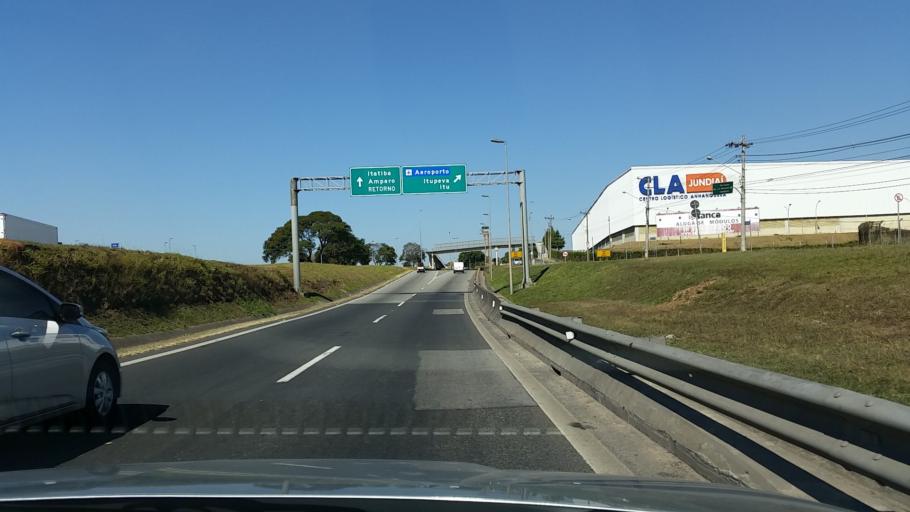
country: BR
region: Sao Paulo
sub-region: Jundiai
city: Jundiai
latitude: -23.1684
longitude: -46.9271
